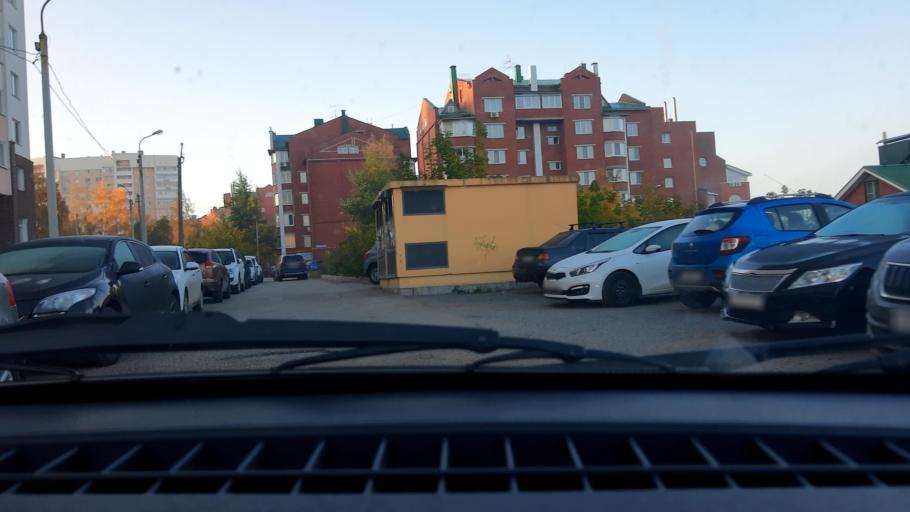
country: RU
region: Bashkortostan
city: Ufa
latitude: 54.7050
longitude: 55.9789
